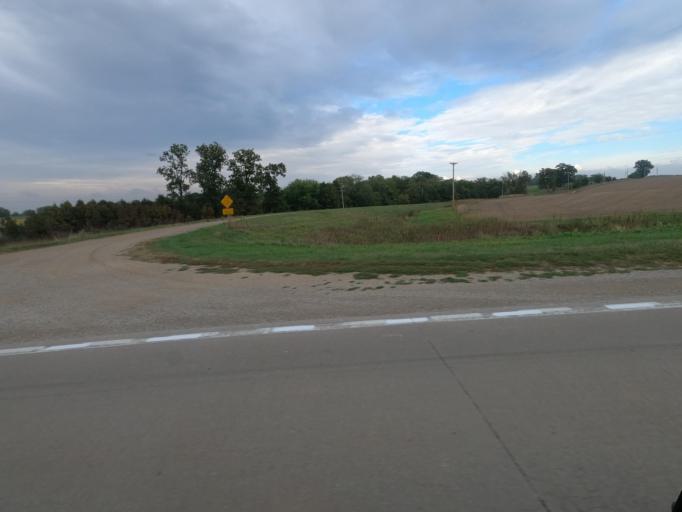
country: US
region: Iowa
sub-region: Henry County
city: Mount Pleasant
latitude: 40.8129
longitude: -91.7050
